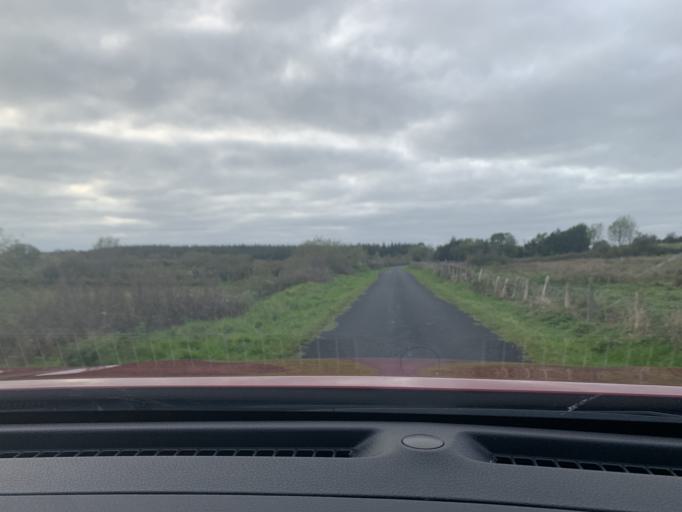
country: IE
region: Connaught
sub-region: Sligo
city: Tobercurry
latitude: 54.0184
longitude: -8.6284
